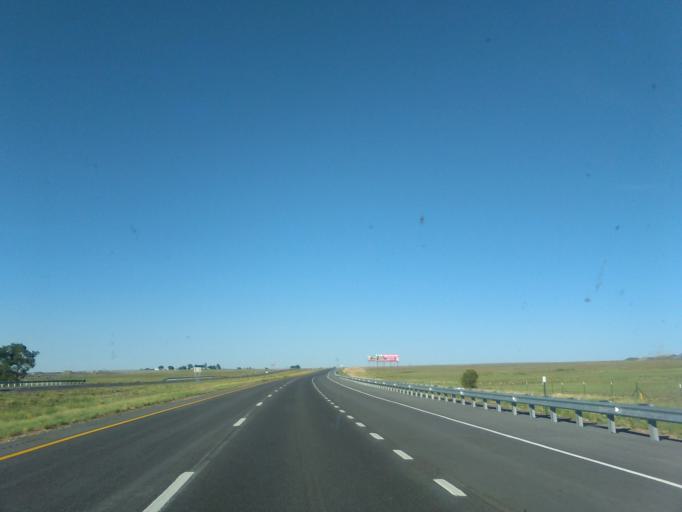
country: US
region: New Mexico
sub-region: San Miguel County
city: Las Vegas
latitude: 35.6792
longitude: -105.1670
